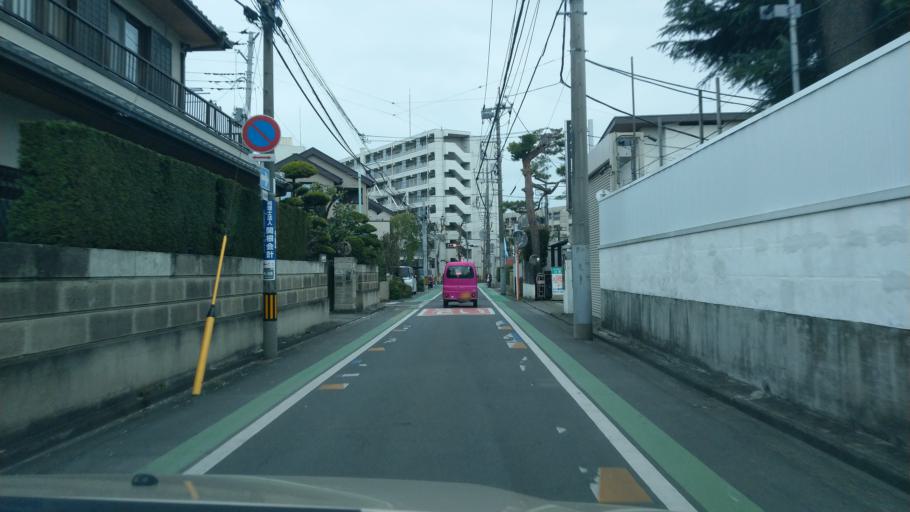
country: JP
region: Saitama
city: Saitama
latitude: 35.9213
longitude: 139.6343
